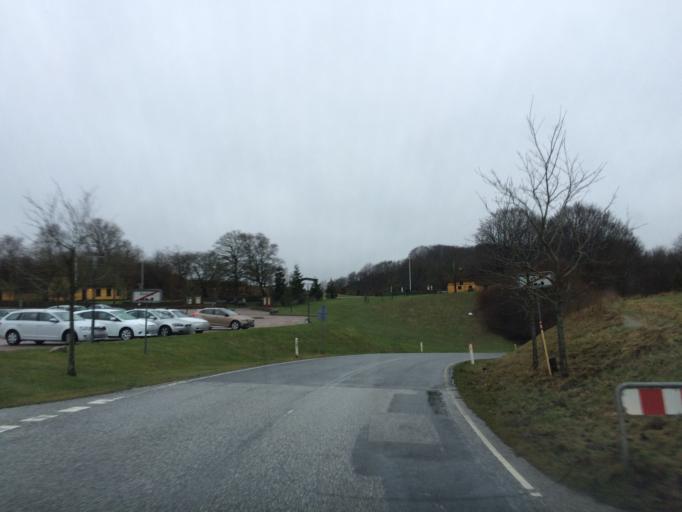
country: DK
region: North Denmark
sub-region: Rebild Kommune
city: Skorping
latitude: 56.8322
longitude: 9.8432
